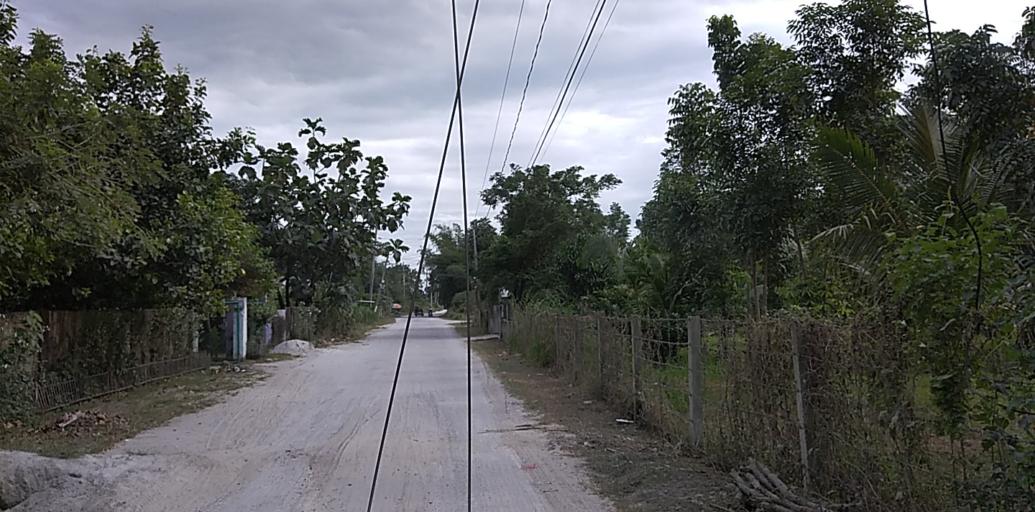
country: PH
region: Central Luzon
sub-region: Province of Pampanga
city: Pulung Santol
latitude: 15.0542
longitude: 120.5603
